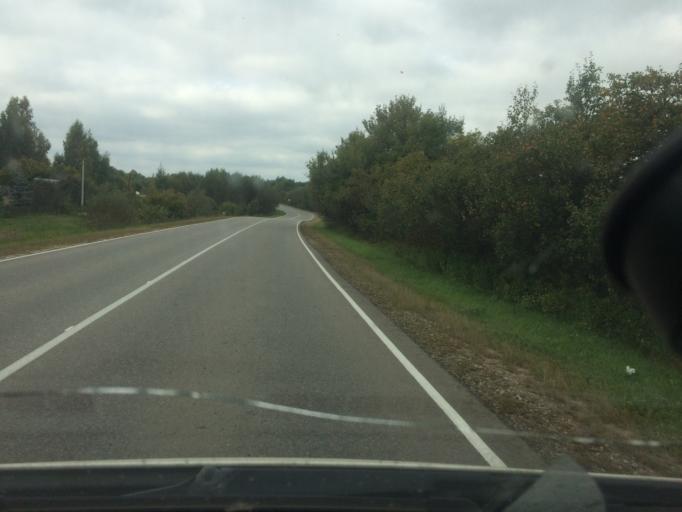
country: RU
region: Tula
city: Odoyev
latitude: 53.9993
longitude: 36.6680
